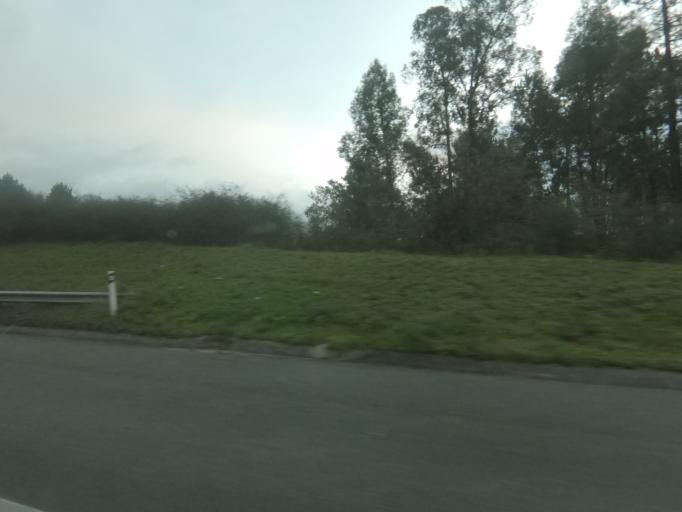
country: PT
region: Braga
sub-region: Vila Verde
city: Prado
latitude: 41.6620
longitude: -8.5483
